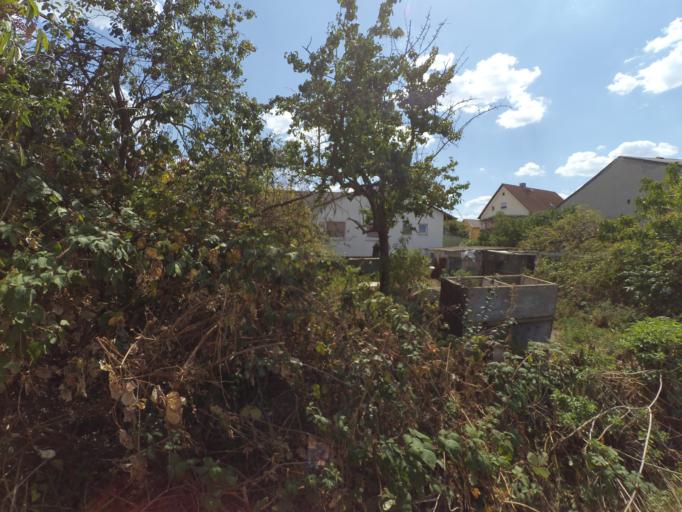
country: DE
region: Hesse
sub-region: Regierungsbezirk Darmstadt
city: Alsbach-Hahnlein
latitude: 49.7406
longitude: 8.5734
